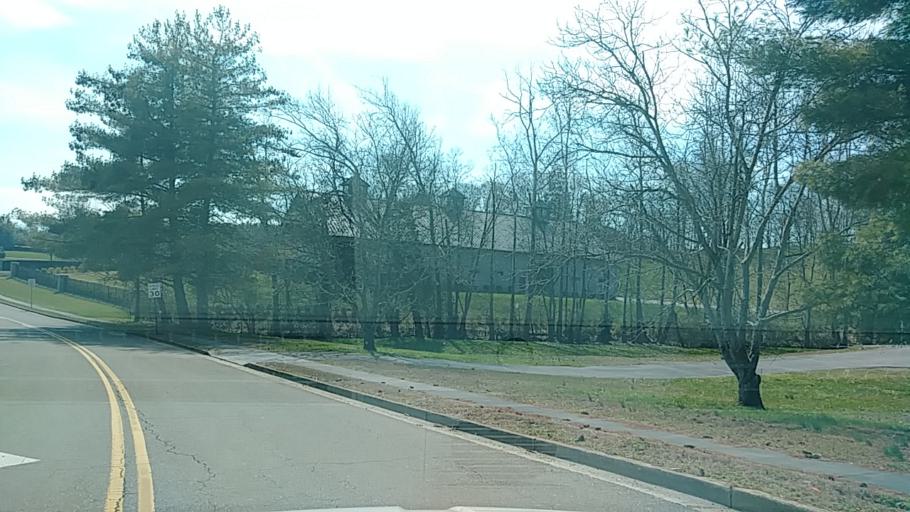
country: US
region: Tennessee
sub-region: Hamblen County
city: Morristown
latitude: 36.2134
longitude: -83.3344
